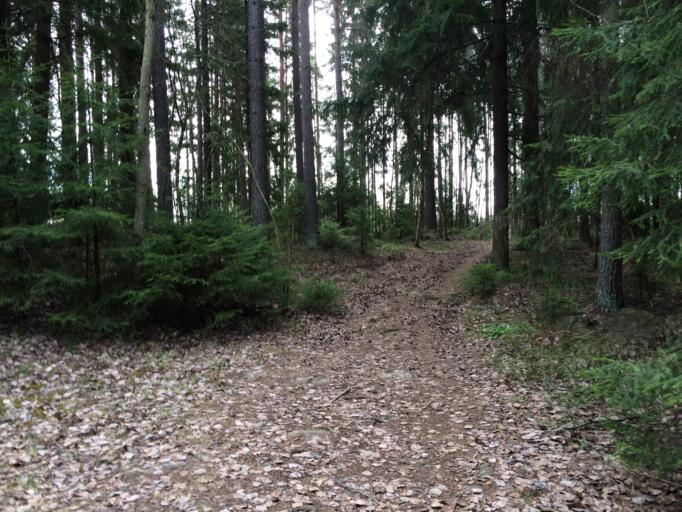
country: SE
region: Vaestmanland
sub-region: Hallstahammars Kommun
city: Hallstahammar
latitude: 59.6262
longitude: 16.2271
